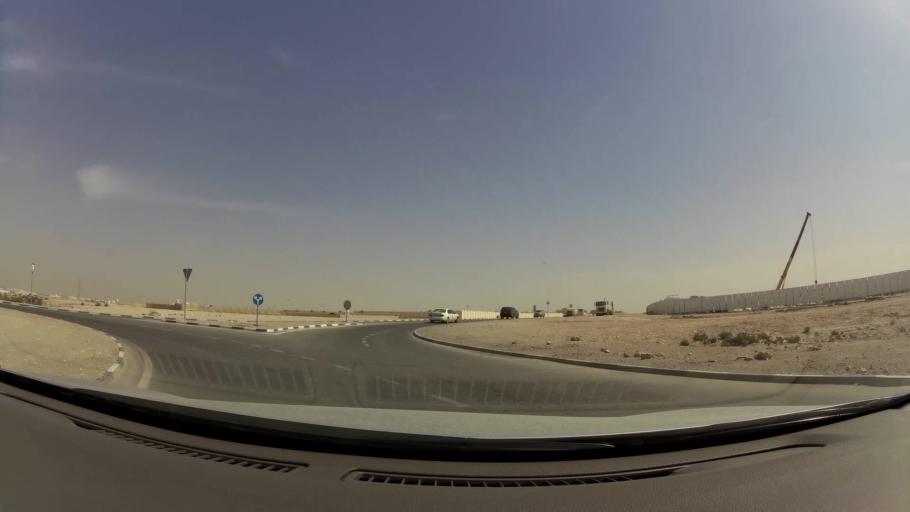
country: QA
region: Baladiyat ar Rayyan
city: Ar Rayyan
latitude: 25.2587
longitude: 51.3826
